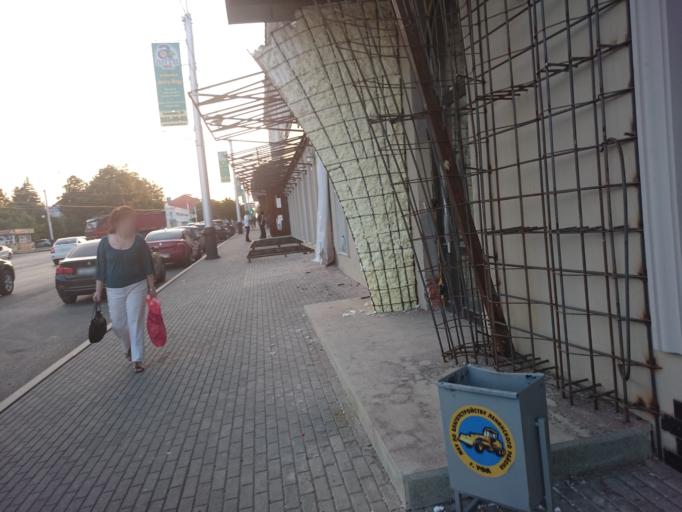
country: RU
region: Bashkortostan
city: Ufa
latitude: 54.7268
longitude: 55.9441
